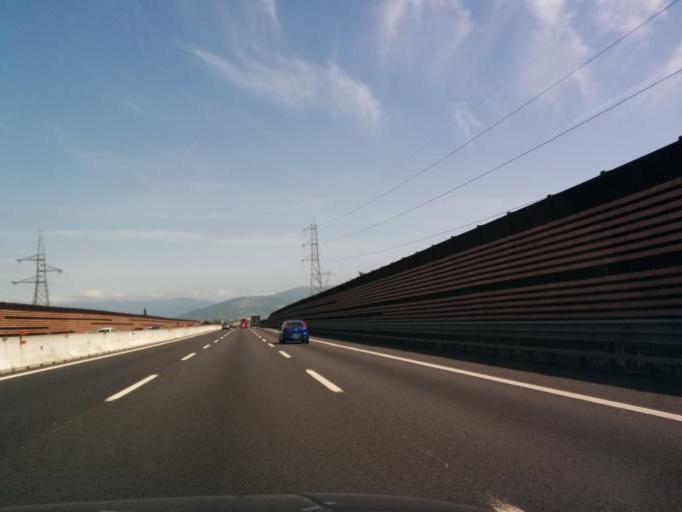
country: IT
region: Tuscany
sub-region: Province of Florence
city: San Donnino
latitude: 43.7930
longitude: 11.1570
